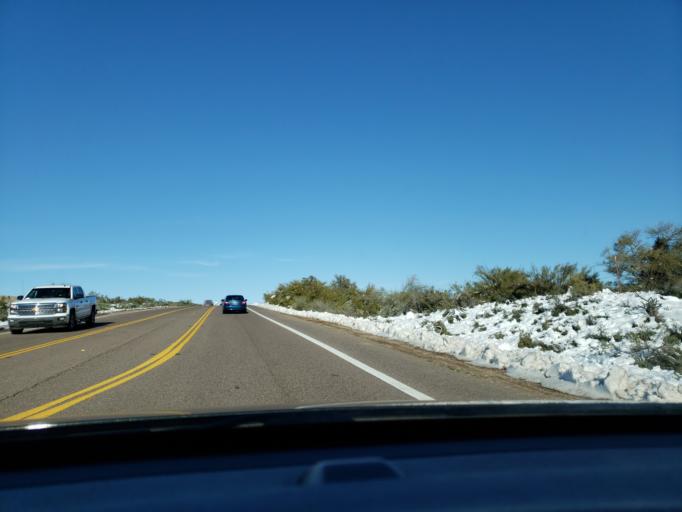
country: US
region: Arizona
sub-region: Maricopa County
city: Carefree
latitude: 33.8458
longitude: -111.8395
